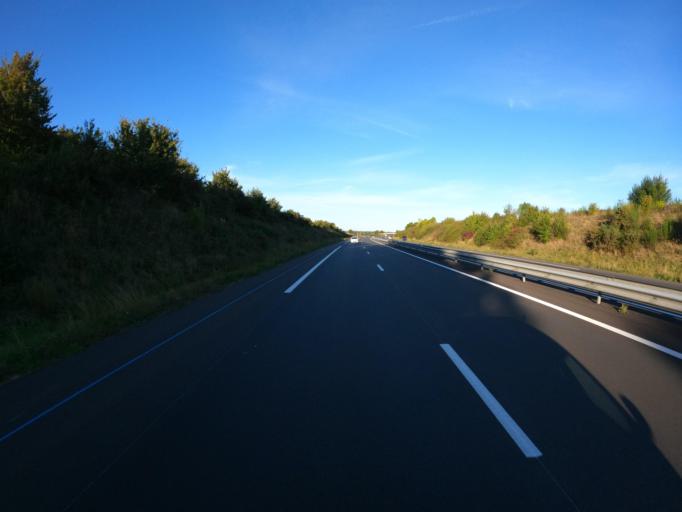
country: FR
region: Pays de la Loire
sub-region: Departement de la Vendee
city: Beaurepaire
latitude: 46.8892
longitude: -1.0988
